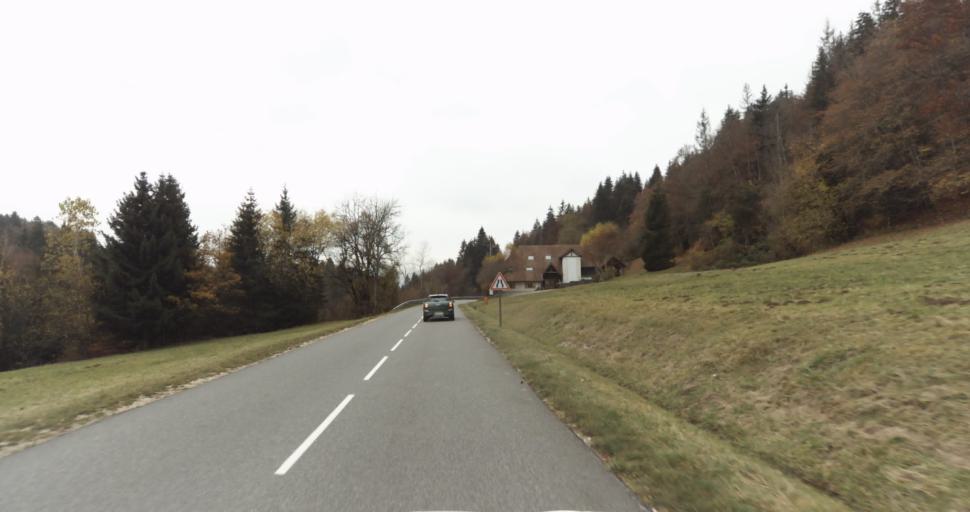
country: FR
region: Rhone-Alpes
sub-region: Departement de la Haute-Savoie
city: Gruffy
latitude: 45.7561
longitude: 6.1173
